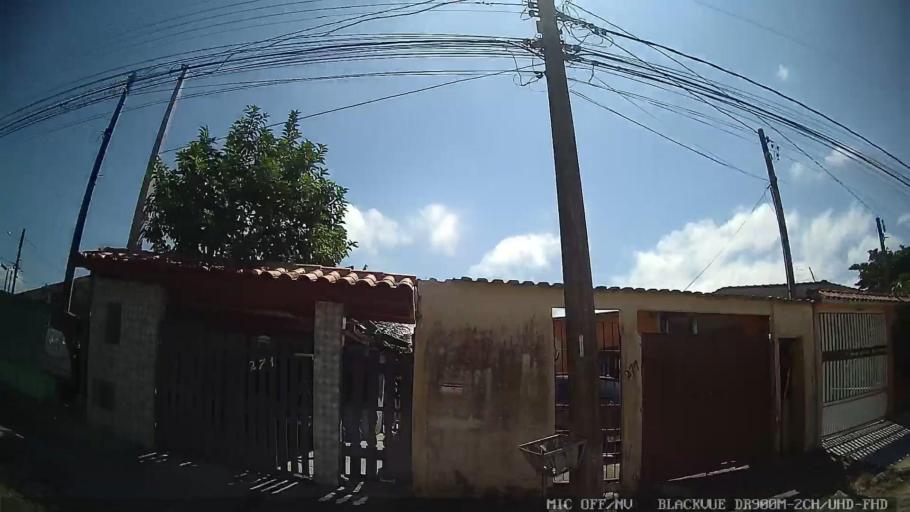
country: BR
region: Sao Paulo
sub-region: Peruibe
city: Peruibe
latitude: -24.3015
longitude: -47.0012
